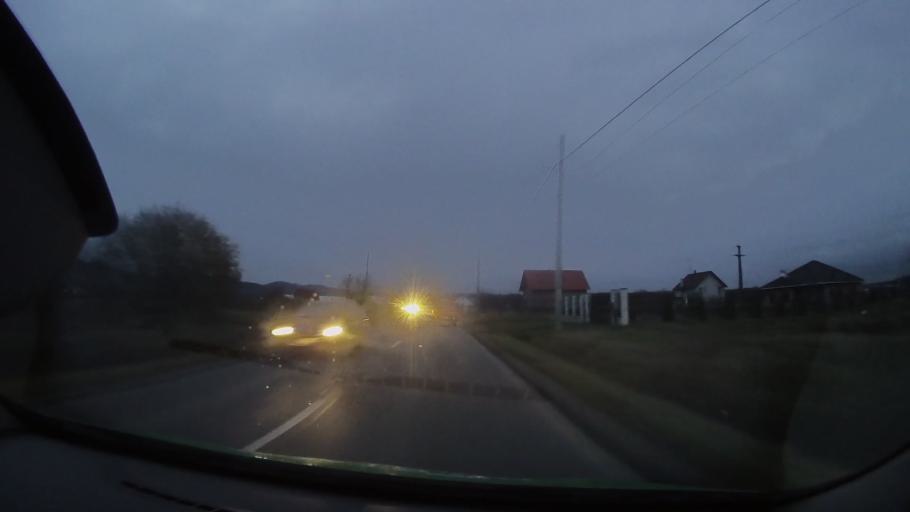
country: RO
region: Mures
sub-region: Comuna Solovastru
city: Solovastru
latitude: 46.7705
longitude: 24.7677
